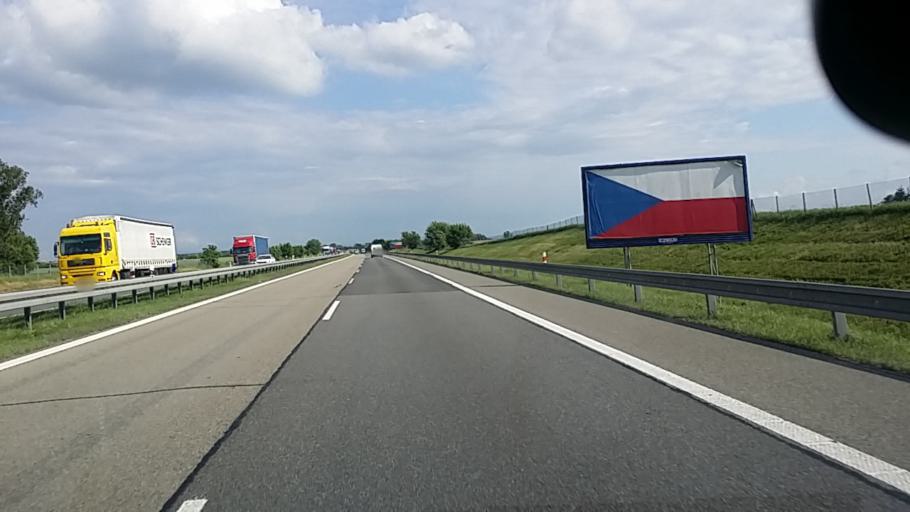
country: CZ
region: South Moravian
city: Kostice
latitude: 48.7583
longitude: 16.9502
